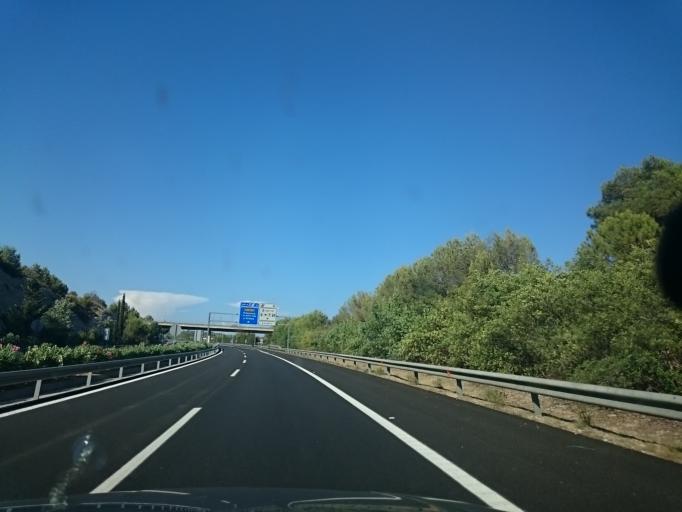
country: ES
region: Catalonia
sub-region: Provincia de Barcelona
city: Cubelles
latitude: 41.2162
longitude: 1.6714
